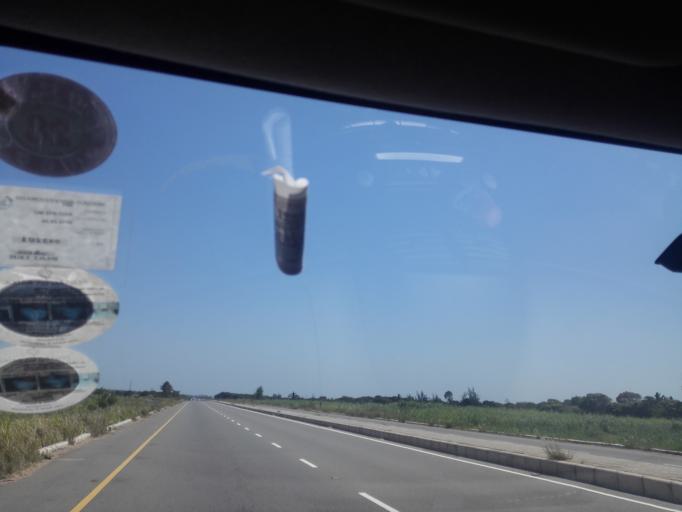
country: MZ
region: Maputo City
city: Maputo
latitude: -25.7992
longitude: 32.6732
